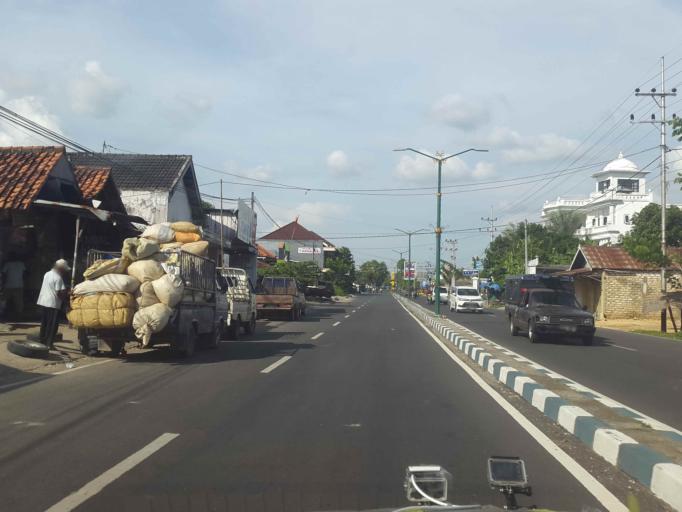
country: ID
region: East Java
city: Sumenep
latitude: -7.0286
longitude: 113.8533
